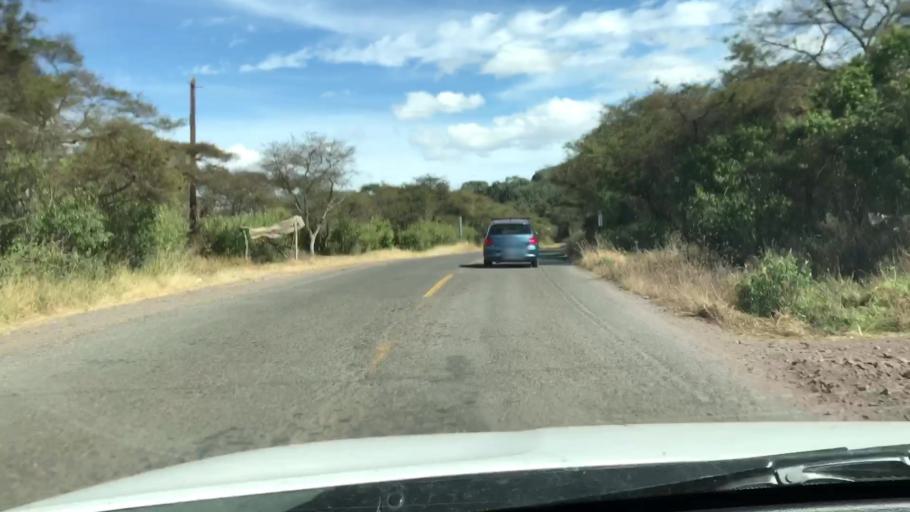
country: MX
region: Jalisco
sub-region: Zacoalco de Torres
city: Barranca de Otates (Barranca de Otatan)
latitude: 20.1951
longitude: -103.7158
